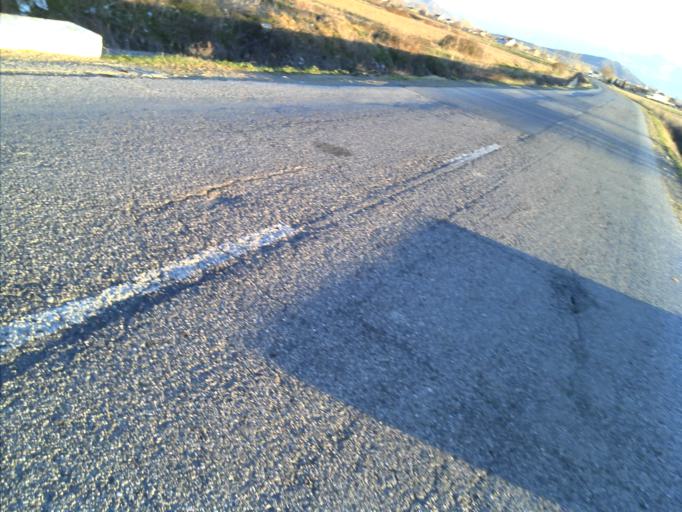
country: AL
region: Shkoder
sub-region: Rrethi i Shkodres
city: Berdica e Madhe
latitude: 41.9663
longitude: 19.4740
